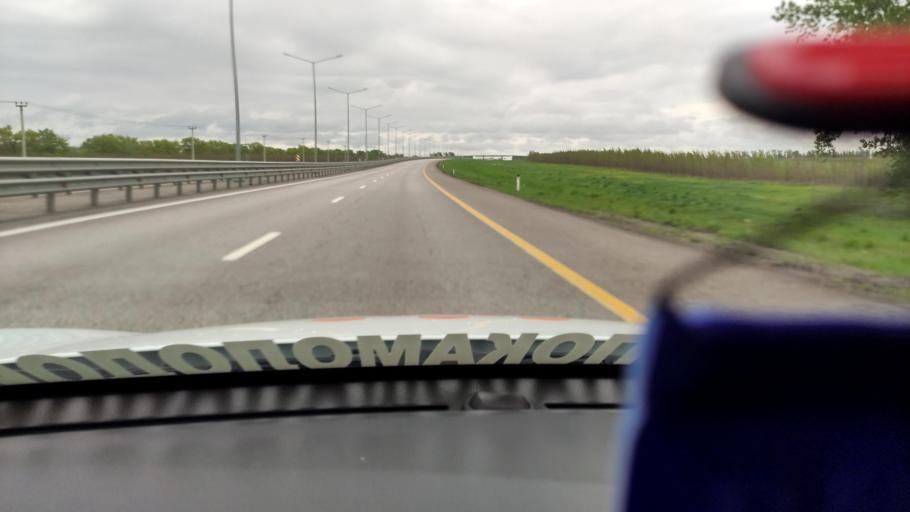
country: RU
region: Voronezj
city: Podkletnoye
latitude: 51.5796
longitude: 39.4627
